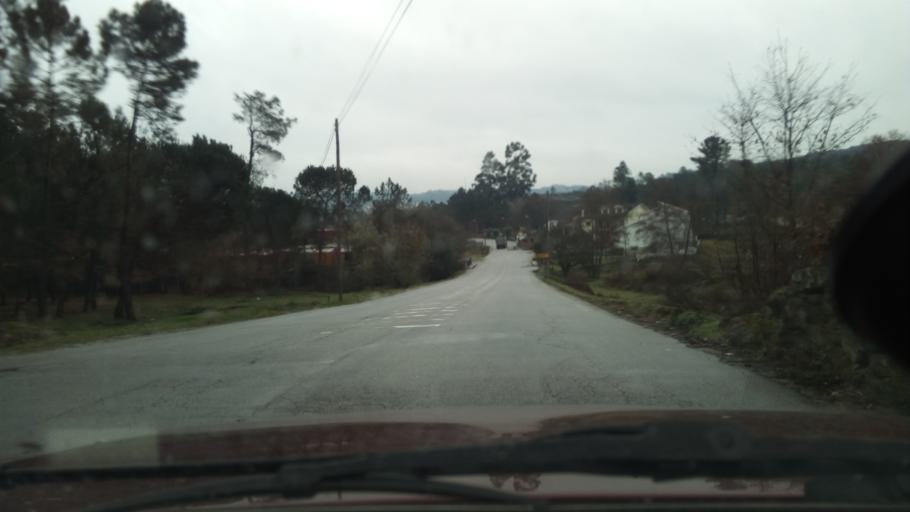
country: PT
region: Viseu
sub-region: Mangualde
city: Mangualde
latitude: 40.6186
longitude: -7.7959
